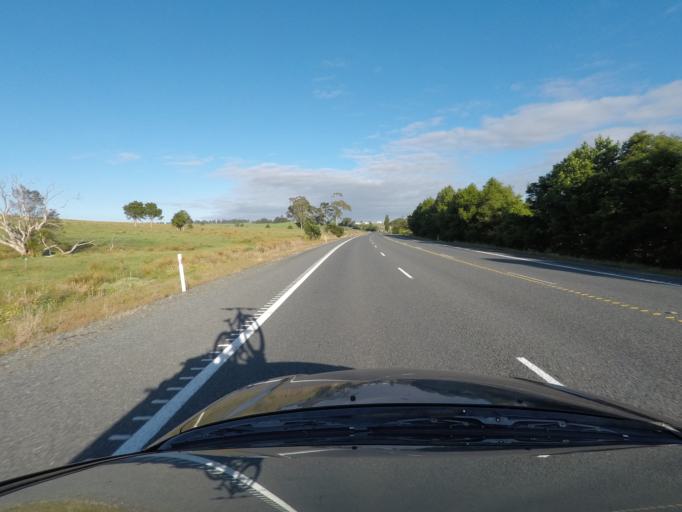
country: NZ
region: Northland
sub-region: Far North District
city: Kawakawa
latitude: -35.5162
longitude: 174.1895
